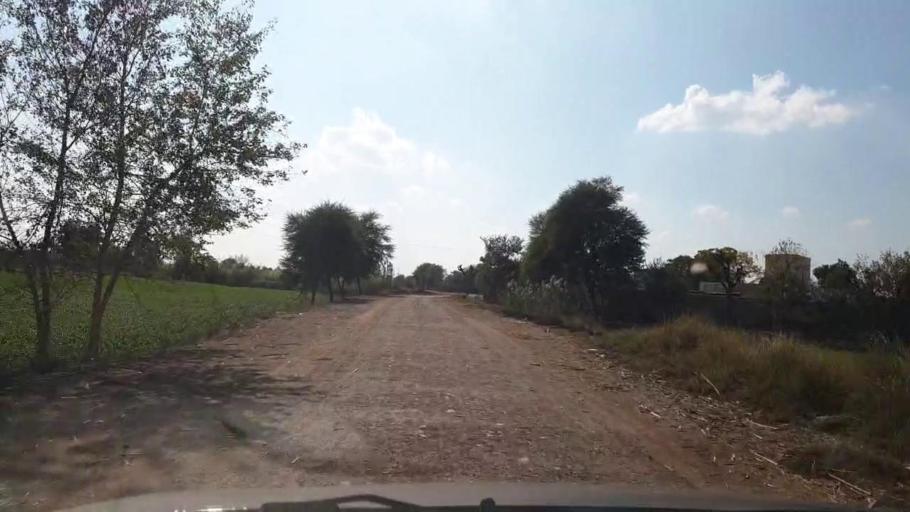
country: PK
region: Sindh
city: Sinjhoro
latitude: 26.0233
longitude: 68.7490
